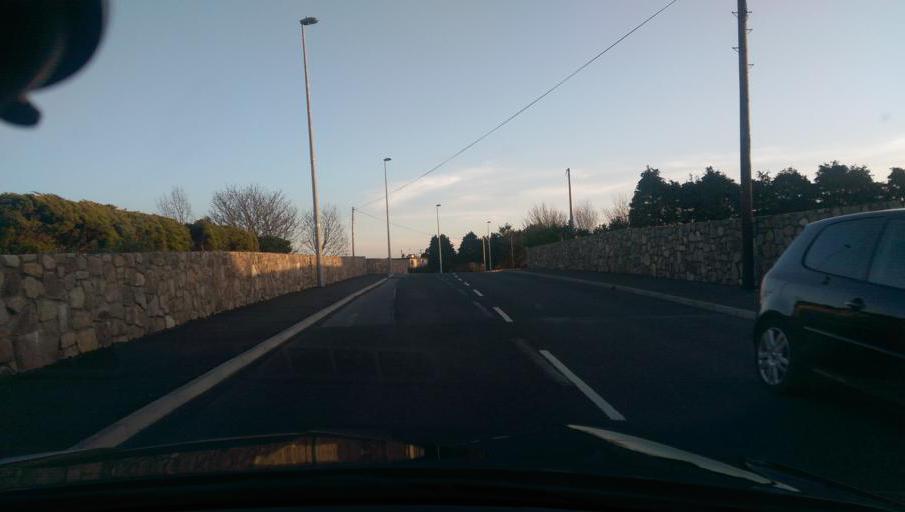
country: IE
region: Connaught
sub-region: County Galway
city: Gaillimh
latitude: 53.2856
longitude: -9.0818
